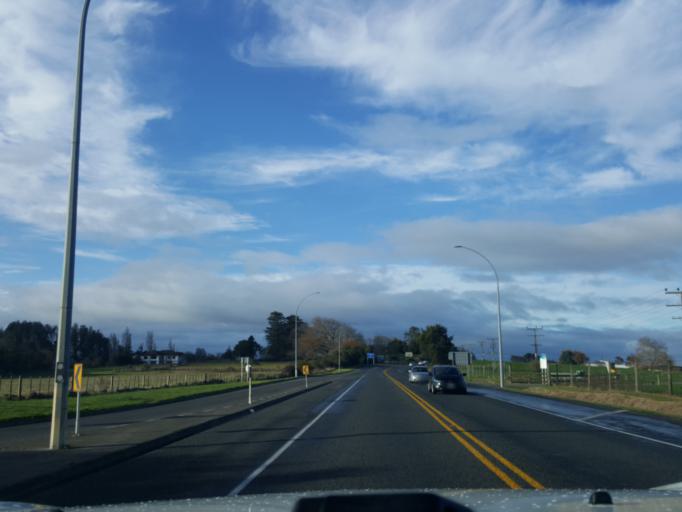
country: NZ
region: Waikato
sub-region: Waikato District
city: Ngaruawahia
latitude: -37.7206
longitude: 175.2156
